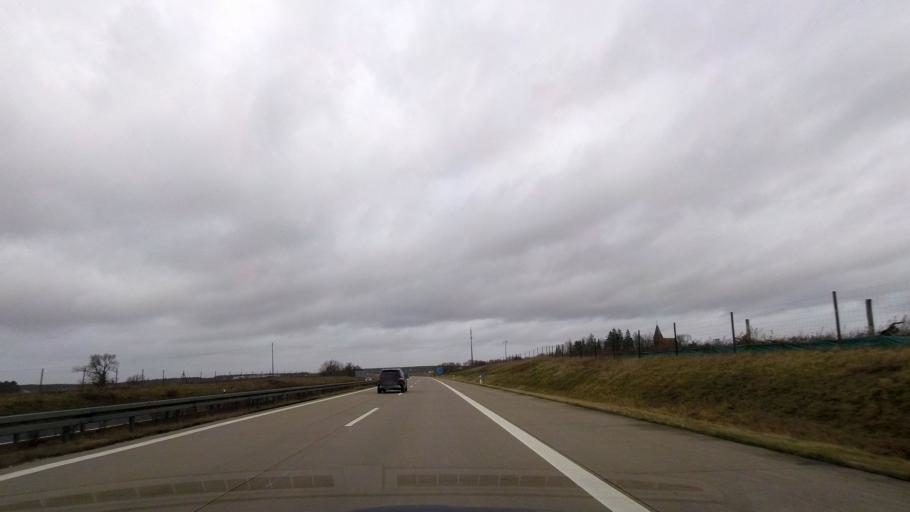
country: DE
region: Mecklenburg-Vorpommern
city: Krakow am See
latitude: 53.6059
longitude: 12.3712
